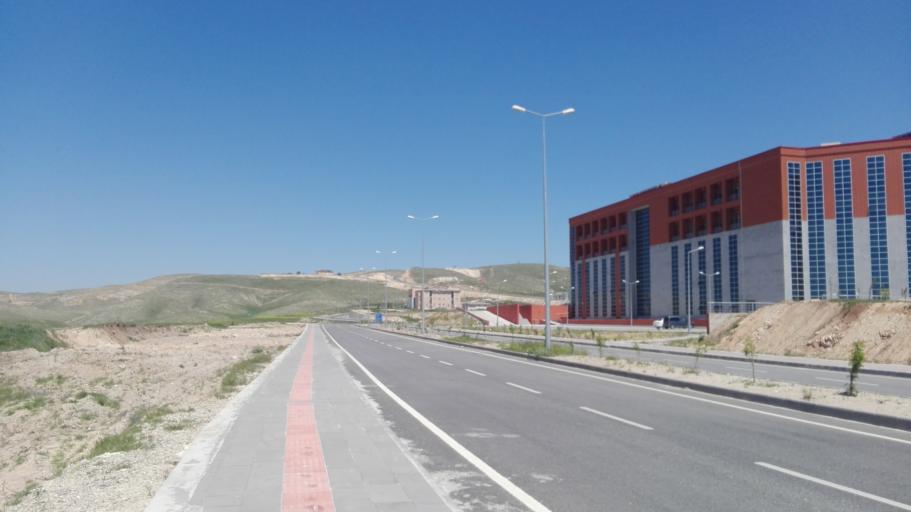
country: TR
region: Batman
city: Oymatas
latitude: 37.7884
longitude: 41.0614
